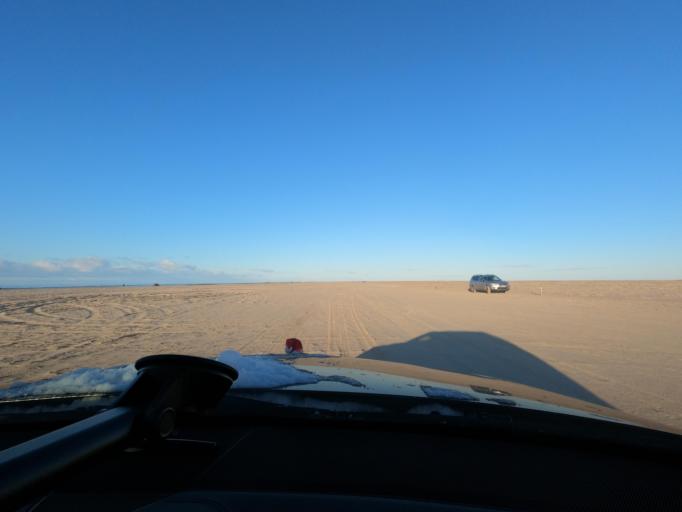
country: DE
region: Schleswig-Holstein
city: List
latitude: 55.1575
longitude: 8.4787
